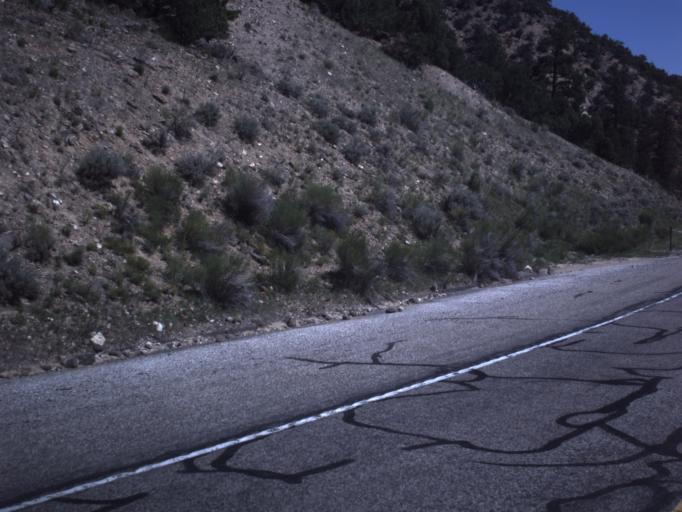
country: US
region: Utah
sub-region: Wayne County
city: Loa
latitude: 38.6595
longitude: -111.4313
